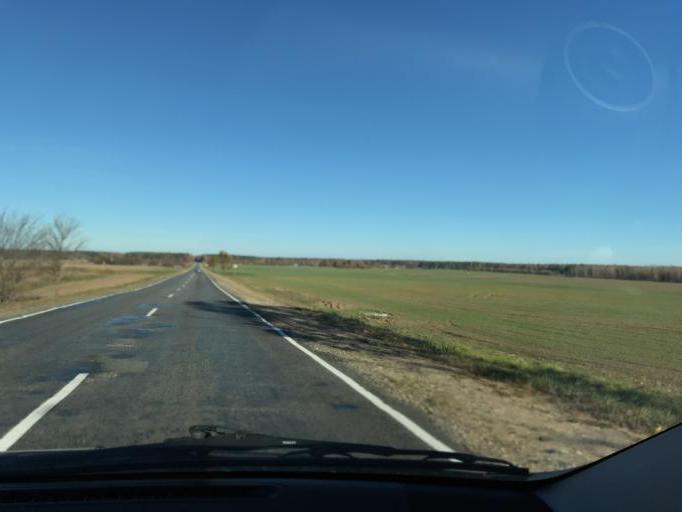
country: BY
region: Vitebsk
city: Lyepyel'
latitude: 55.0443
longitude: 28.7498
